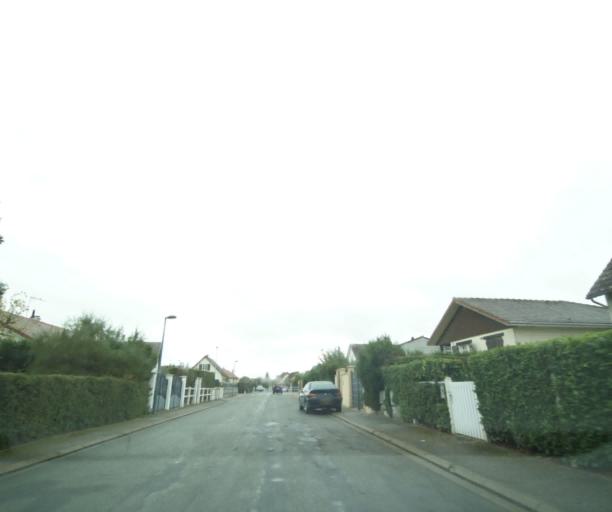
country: FR
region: Centre
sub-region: Departement d'Eure-et-Loir
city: Vernouillet
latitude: 48.7219
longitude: 1.3789
